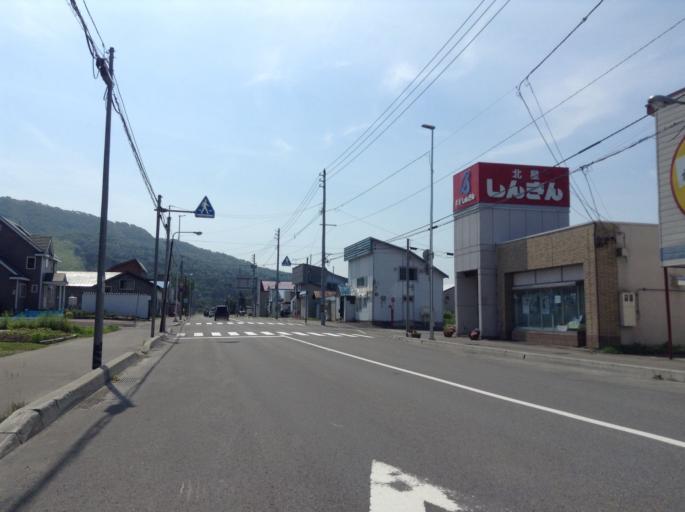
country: JP
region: Hokkaido
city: Nayoro
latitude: 44.7276
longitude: 142.2593
